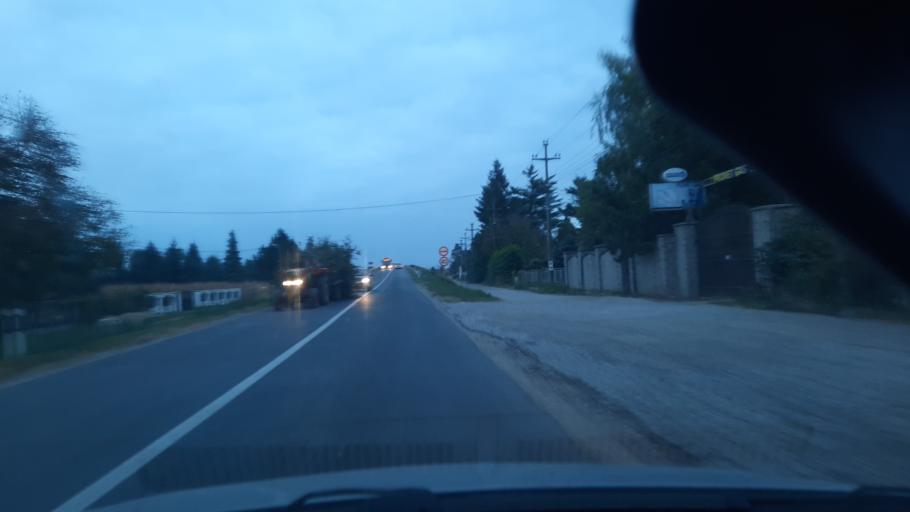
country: RS
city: Zvecka
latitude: 44.6509
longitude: 20.1528
